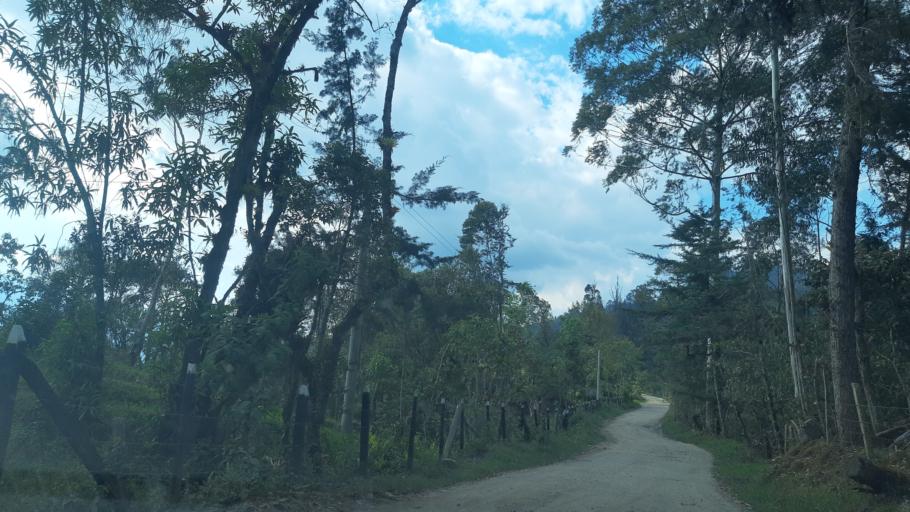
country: CO
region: Boyaca
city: Garagoa
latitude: 5.0876
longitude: -73.3358
